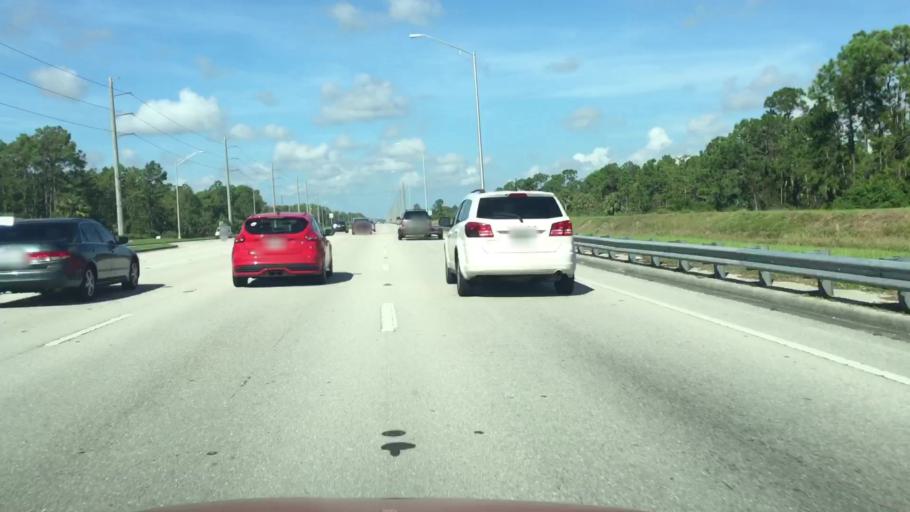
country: US
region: Florida
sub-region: Collier County
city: Orangetree
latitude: 26.2766
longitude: -81.6145
